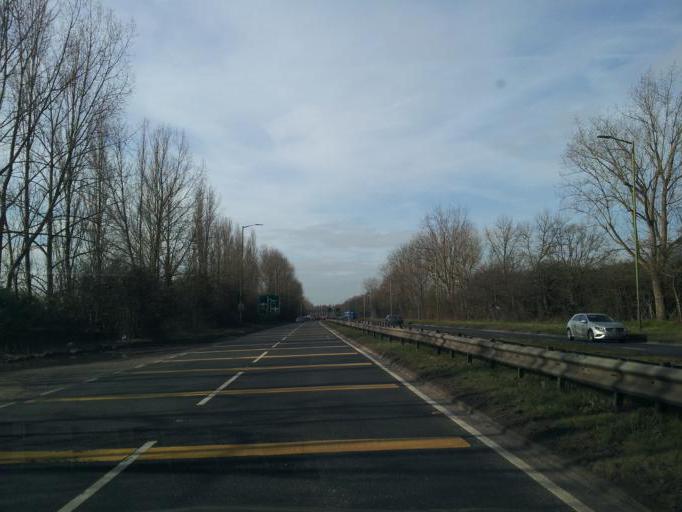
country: GB
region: England
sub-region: Hertfordshire
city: Hatfield
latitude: 51.7451
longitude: -0.2620
